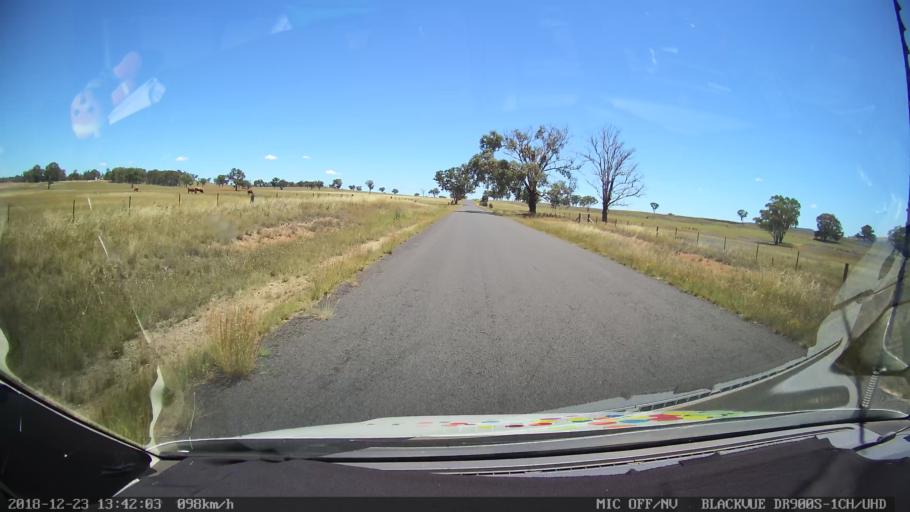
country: AU
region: New South Wales
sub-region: Armidale Dumaresq
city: Armidale
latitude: -30.4726
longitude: 151.1670
